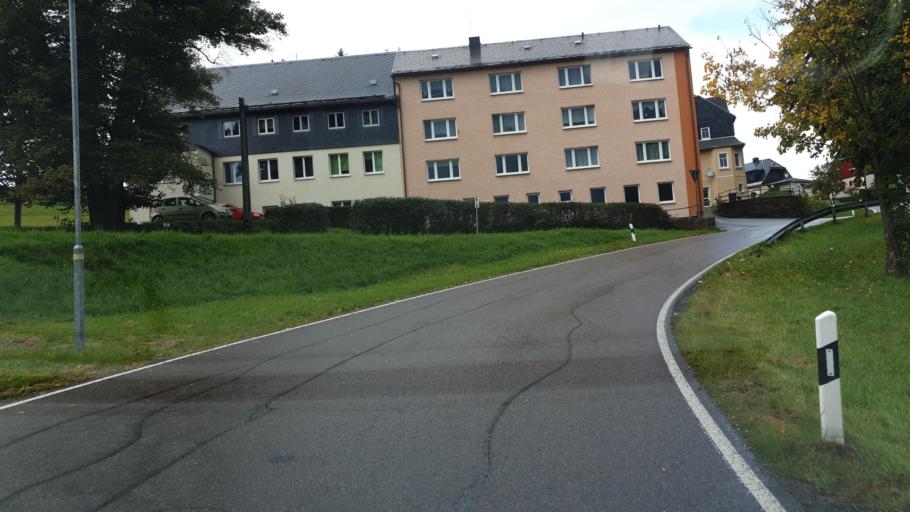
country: DE
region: Saxony
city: Neuhausen
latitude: 50.6938
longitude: 13.4867
